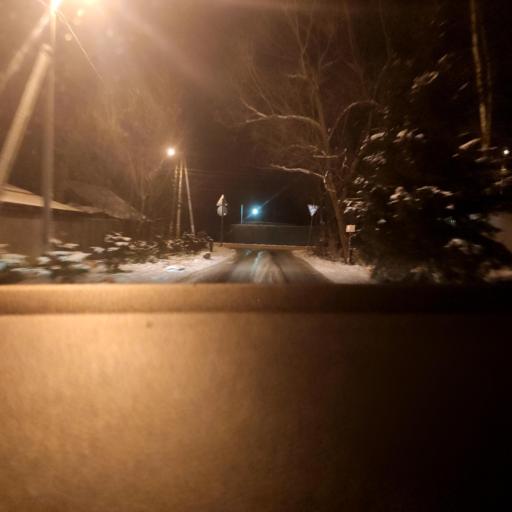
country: RU
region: Moskovskaya
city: Zhavoronki
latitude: 55.6358
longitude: 37.0869
